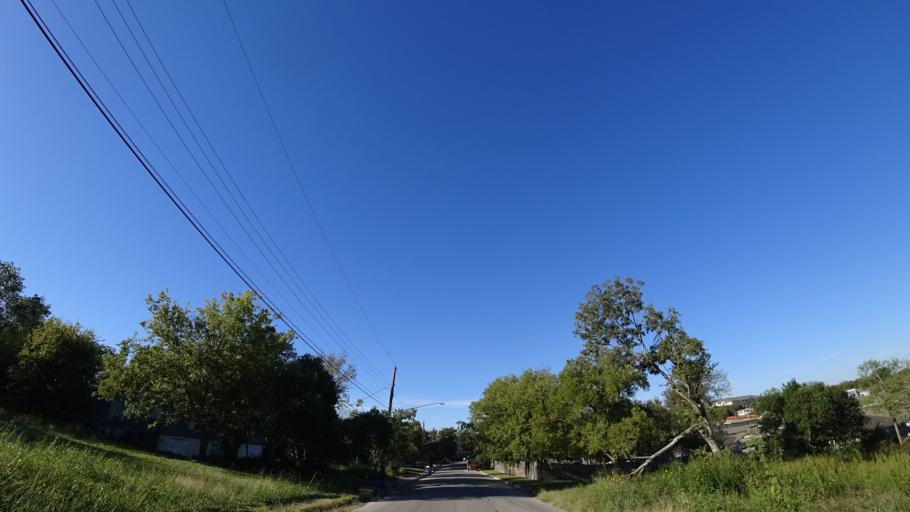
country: US
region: Texas
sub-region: Travis County
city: Austin
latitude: 30.2189
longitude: -97.6973
